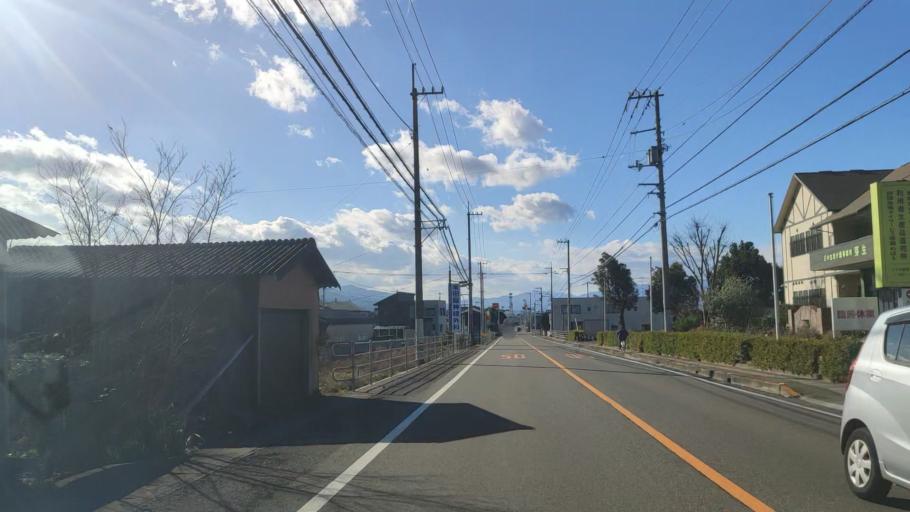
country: JP
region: Ehime
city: Saijo
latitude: 33.9148
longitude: 133.2140
